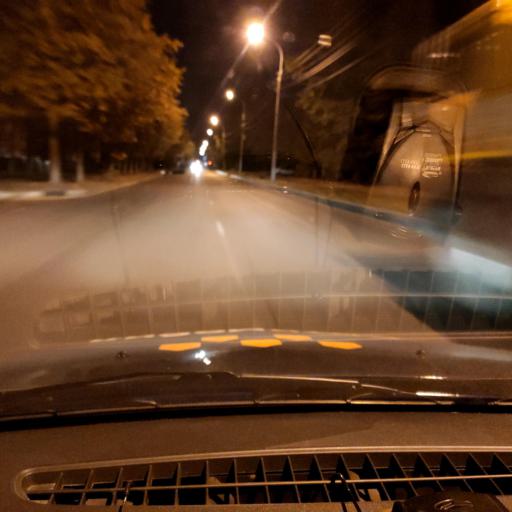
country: RU
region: Voronezj
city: Voronezh
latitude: 51.6550
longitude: 39.1477
